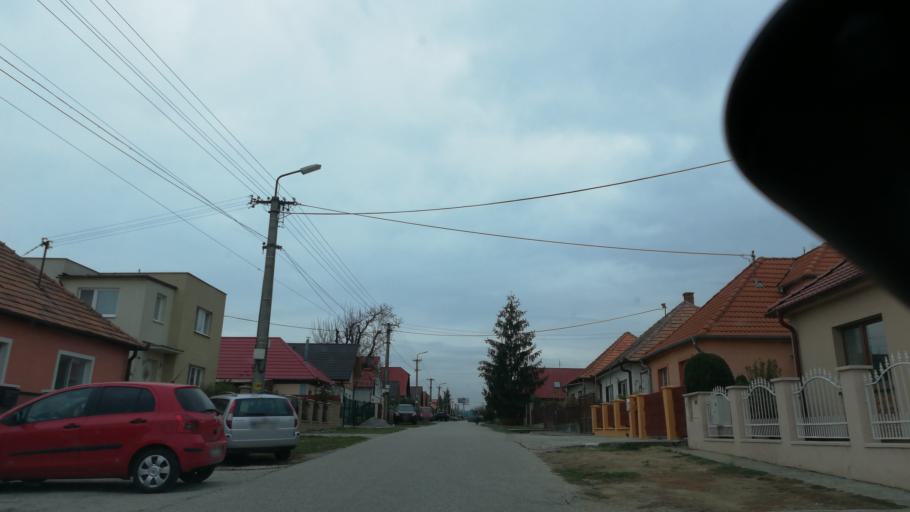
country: SK
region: Nitriansky
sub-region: Okres Nitra
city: Nitra
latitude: 48.3173
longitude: 17.9891
